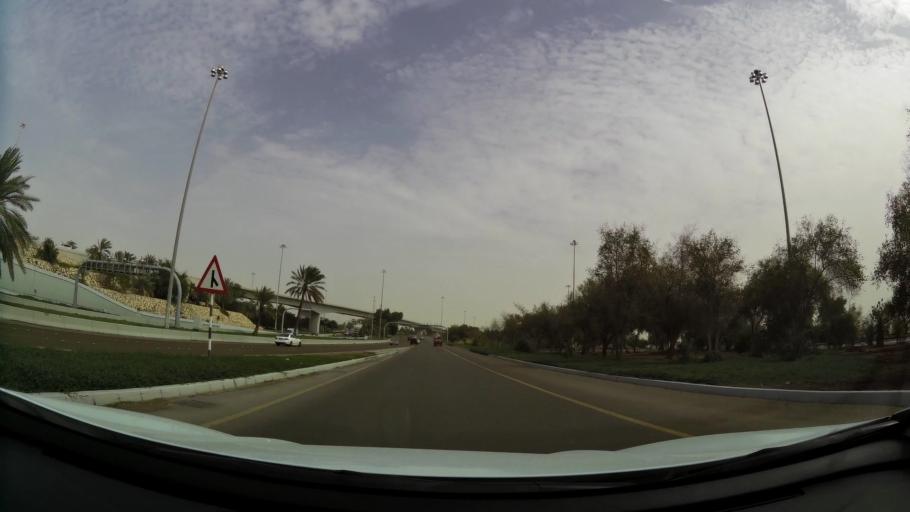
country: AE
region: Abu Dhabi
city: Abu Dhabi
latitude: 24.3901
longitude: 54.5334
